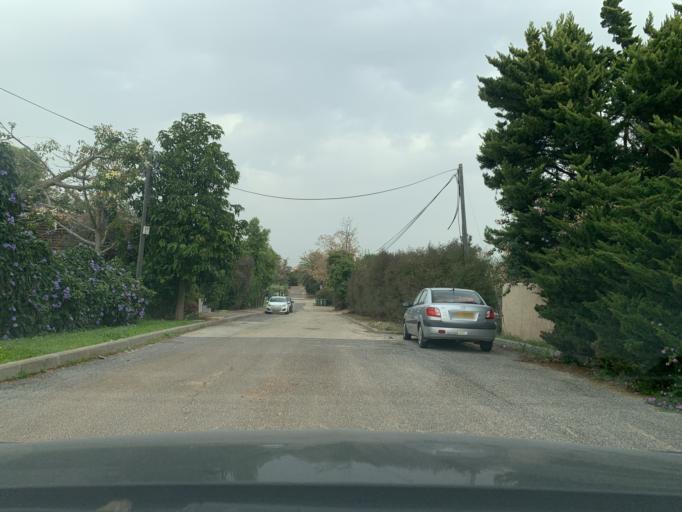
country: IL
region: Central District
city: Kfar Saba
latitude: 32.1952
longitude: 34.9045
